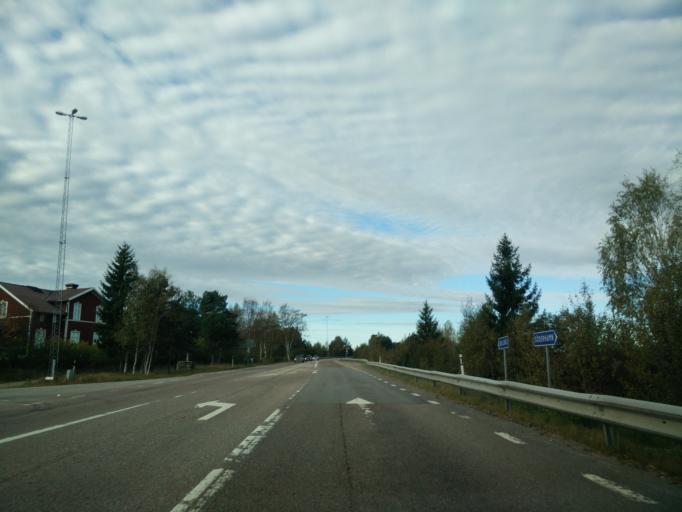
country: SE
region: Gaevleborg
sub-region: Soderhamns Kommun
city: Soderhamn
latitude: 61.2863
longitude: 16.9202
